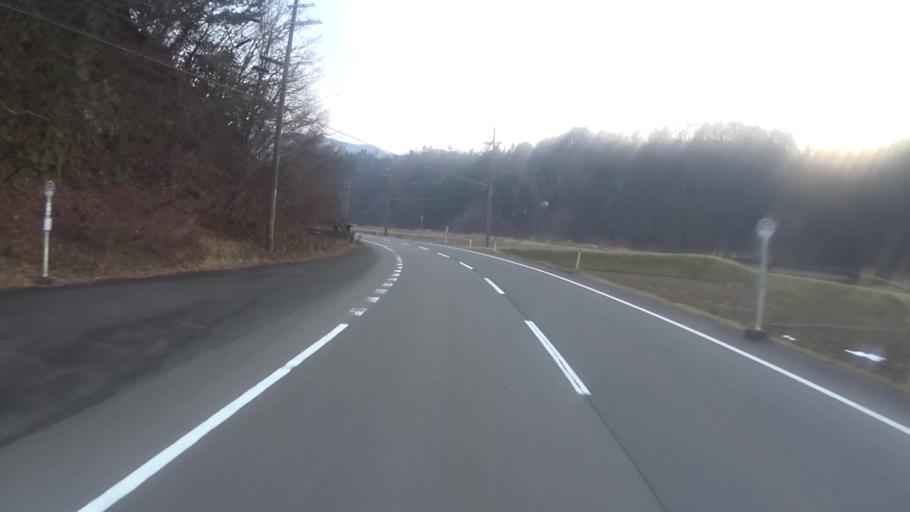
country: JP
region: Kyoto
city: Maizuru
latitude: 35.3951
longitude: 135.4636
